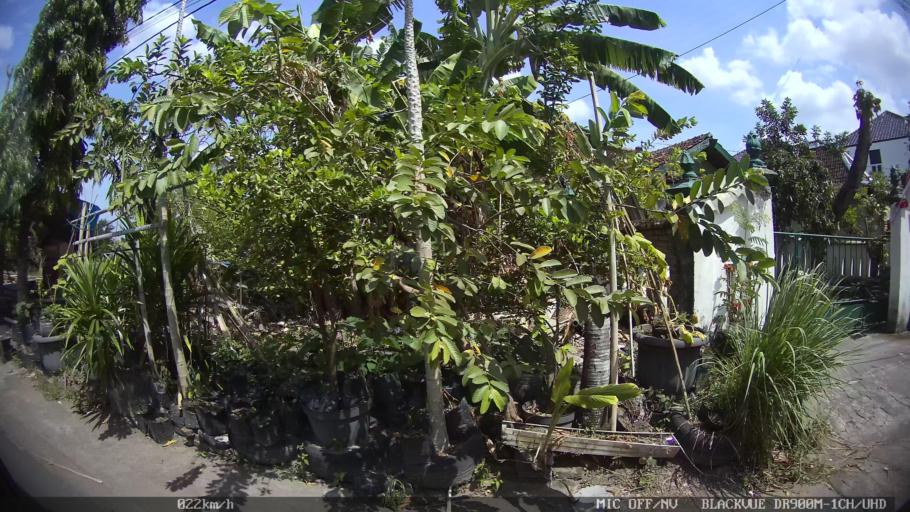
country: ID
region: Daerah Istimewa Yogyakarta
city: Sewon
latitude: -7.8328
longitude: 110.3863
